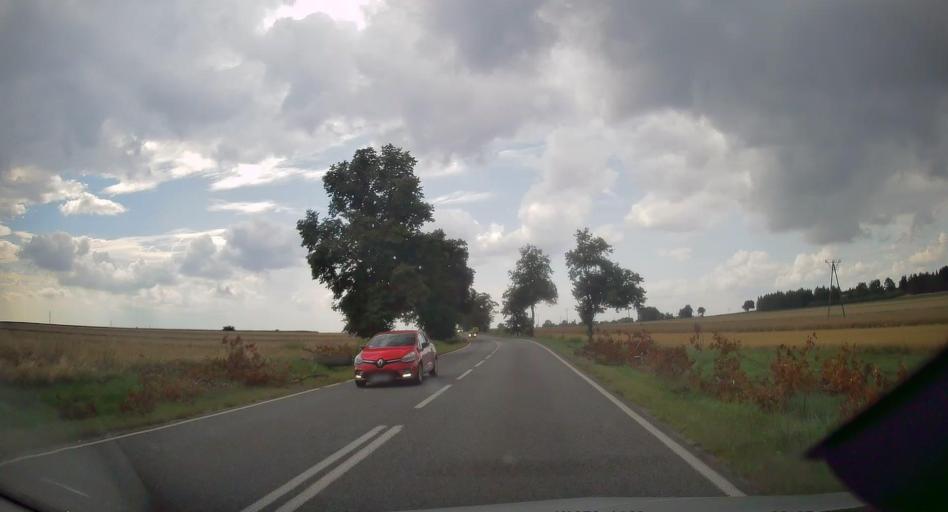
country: PL
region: Lodz Voivodeship
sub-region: Powiat skierniewicki
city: Gluchow
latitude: 51.7770
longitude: 20.1143
